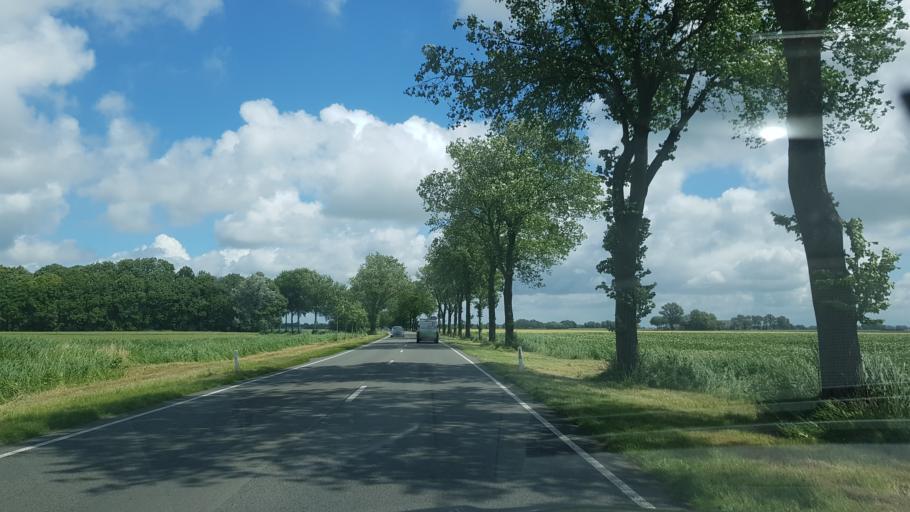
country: NL
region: Groningen
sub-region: Gemeente Bedum
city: Bedum
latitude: 53.4065
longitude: 6.6297
